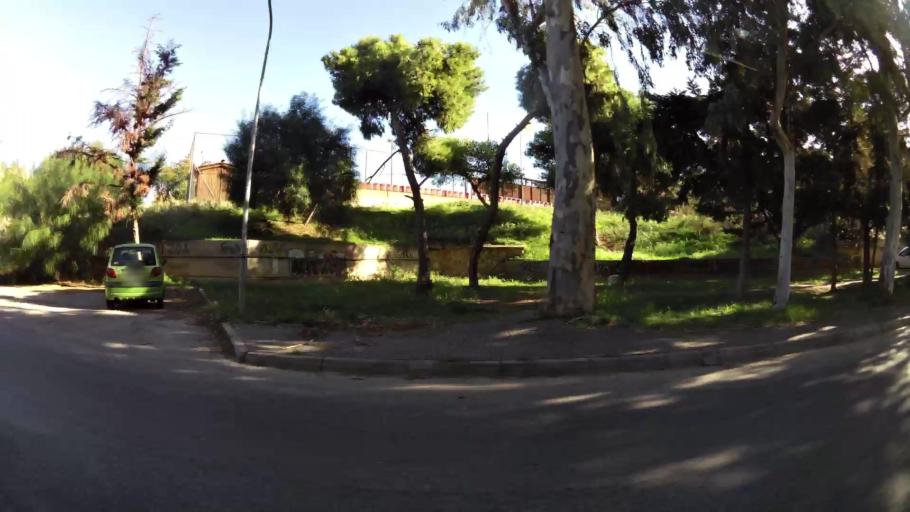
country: GR
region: Attica
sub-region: Nomarchia Athinas
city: Elliniko
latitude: 37.8697
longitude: 23.7421
